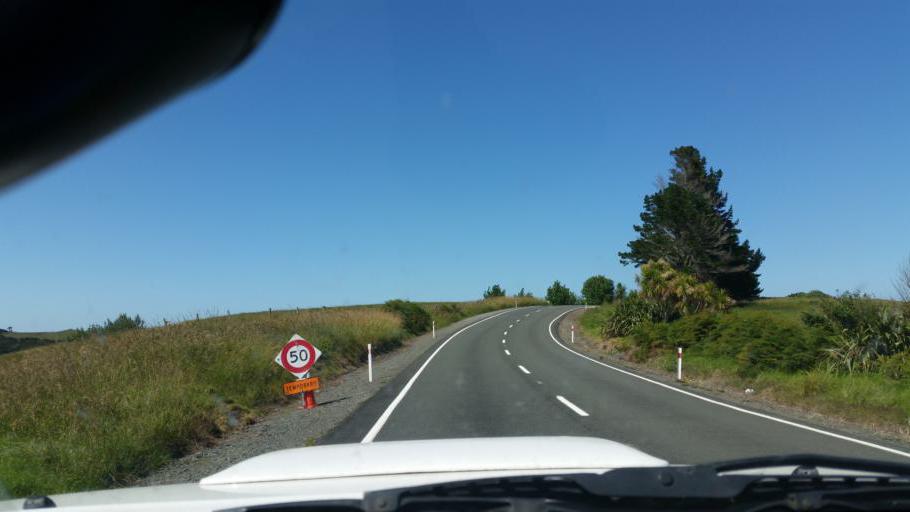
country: NZ
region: Auckland
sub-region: Auckland
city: Wellsford
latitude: -36.2224
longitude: 174.3792
